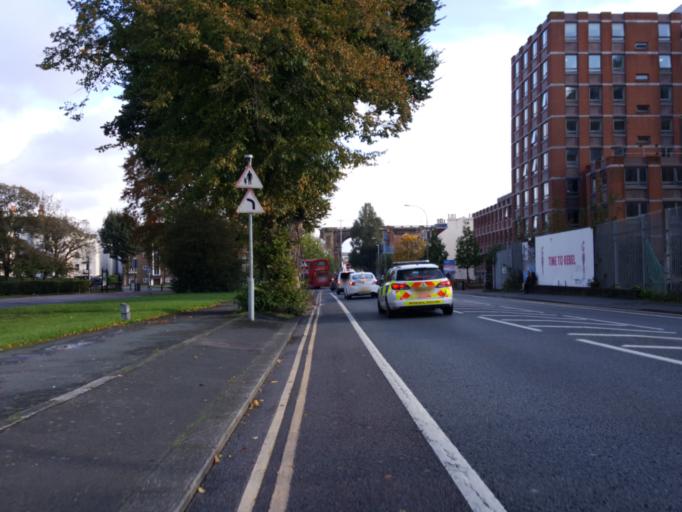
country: GB
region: England
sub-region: Brighton and Hove
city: Brighton
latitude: 50.8370
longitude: -0.1445
